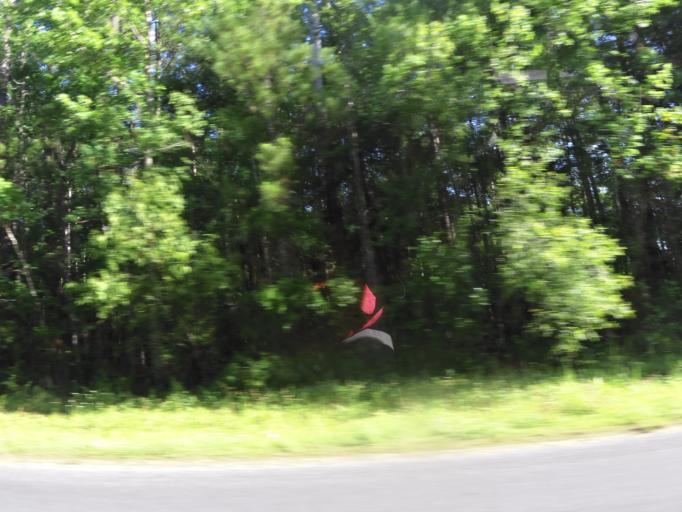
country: US
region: Florida
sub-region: Nassau County
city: Nassau Village-Ratliff
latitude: 30.5108
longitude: -81.7944
